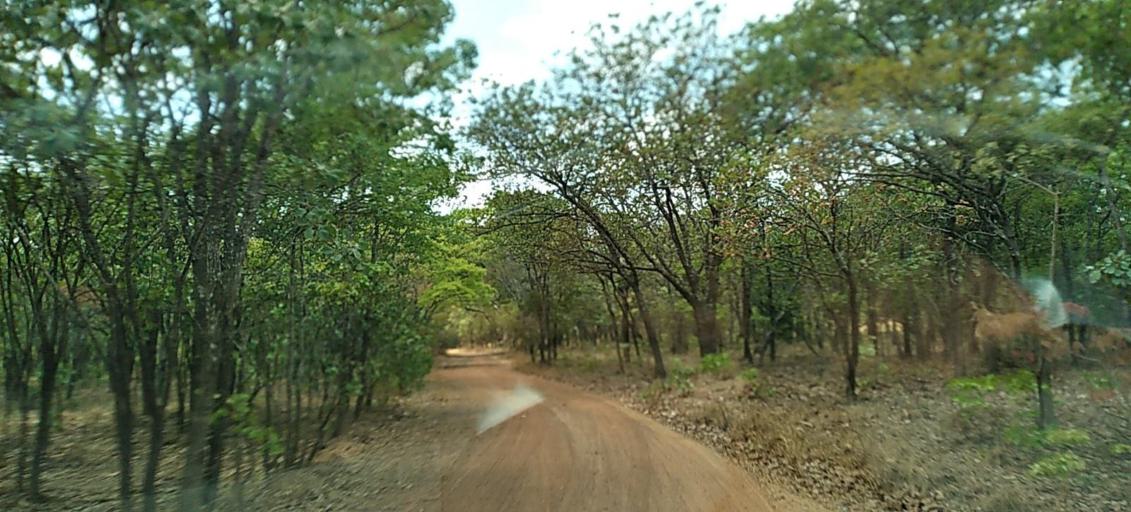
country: ZM
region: Copperbelt
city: Chililabombwe
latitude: -12.5057
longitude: 27.6349
